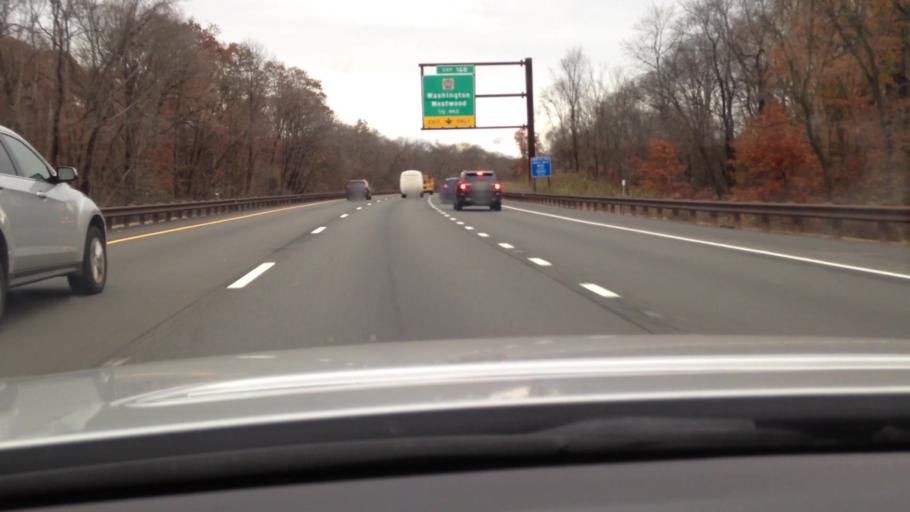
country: US
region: New Jersey
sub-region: Bergen County
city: Ho-Ho-Kus
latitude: 40.9896
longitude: -74.0729
